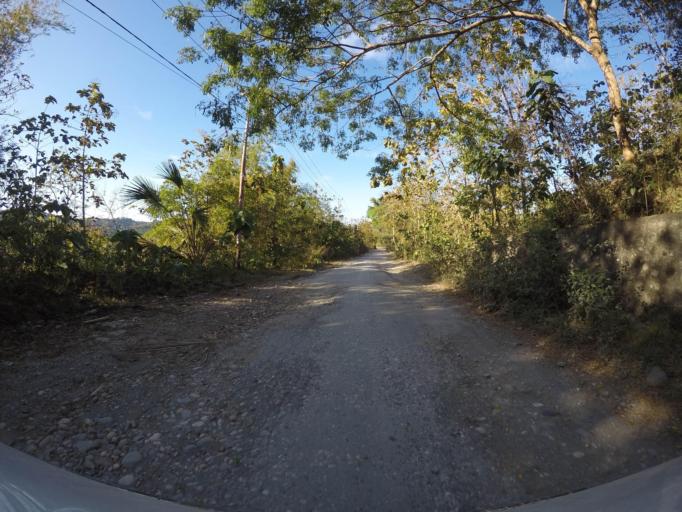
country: TL
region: Viqueque
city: Viqueque
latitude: -8.8754
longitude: 126.3245
